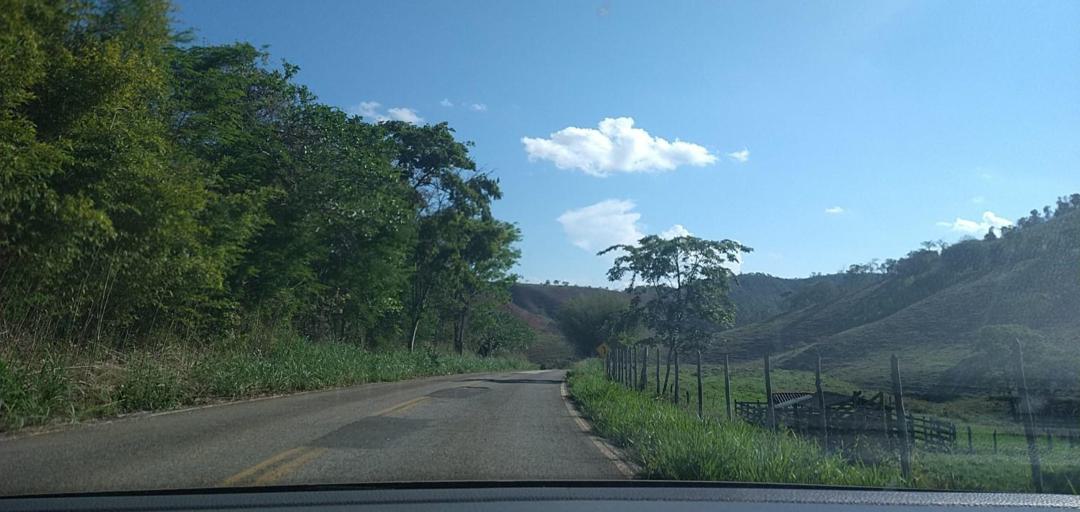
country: BR
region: Minas Gerais
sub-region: Alvinopolis
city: Alvinopolis
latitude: -20.1991
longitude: -42.9277
